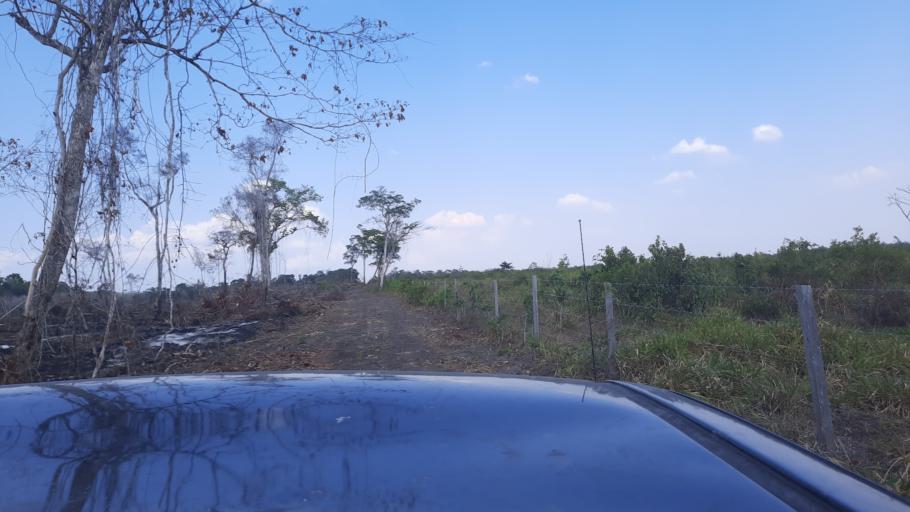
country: BZ
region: Cayo
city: Valley of Peace
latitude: 17.4041
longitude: -89.0376
